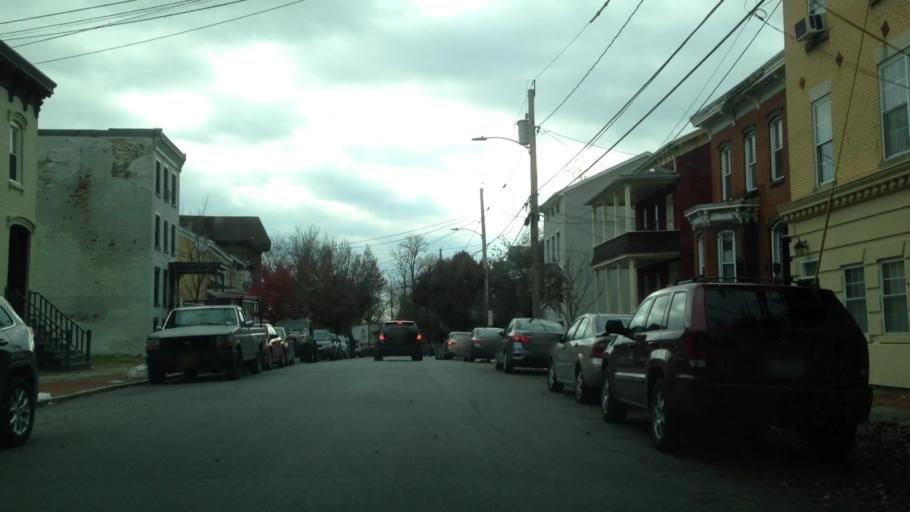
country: US
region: New York
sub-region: Dutchess County
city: Poughkeepsie
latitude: 41.7055
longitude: -73.9356
